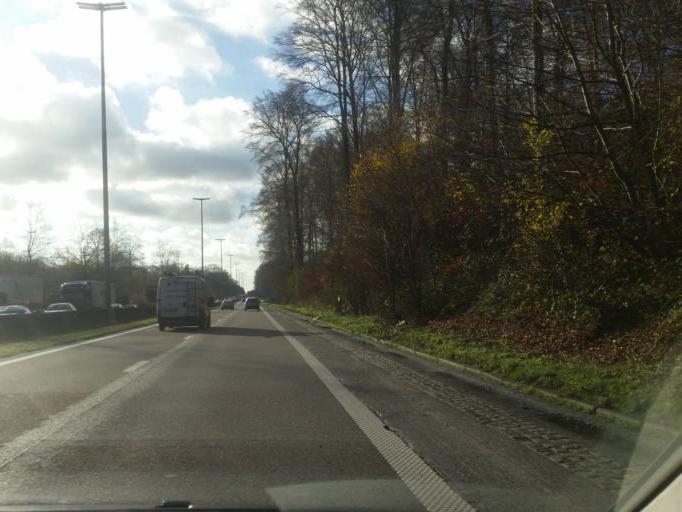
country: BE
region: Flanders
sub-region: Provincie Vlaams-Brabant
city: Hoeilaart
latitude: 50.7901
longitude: 4.4576
